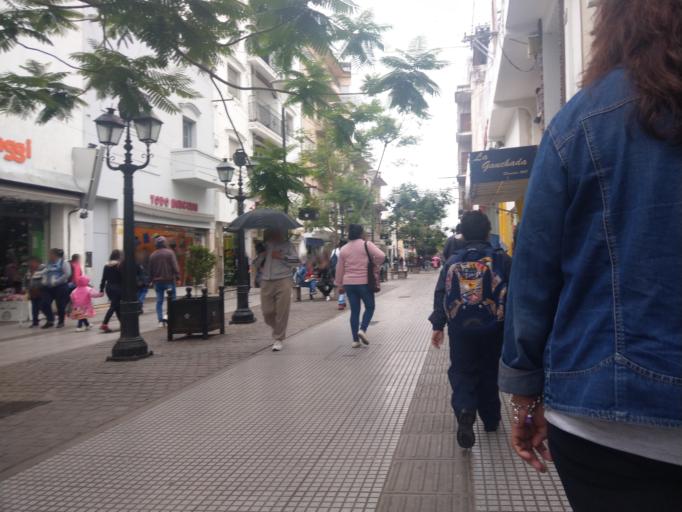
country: AR
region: Salta
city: Salta
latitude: -24.7912
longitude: -65.4126
